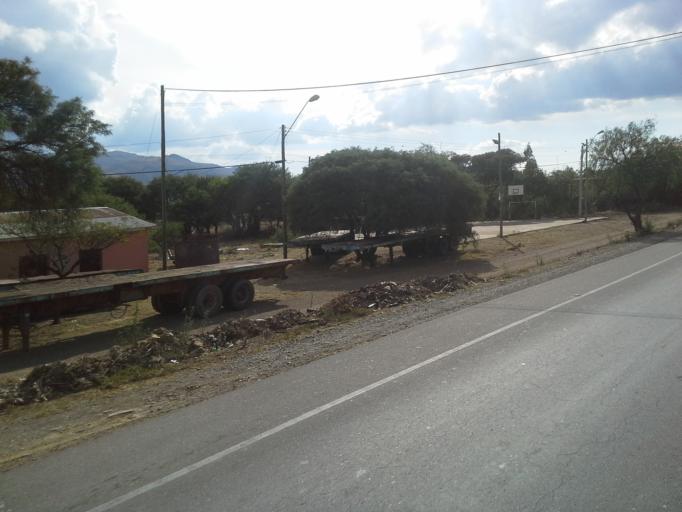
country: BO
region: Cochabamba
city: Tarata
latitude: -17.5390
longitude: -66.0683
